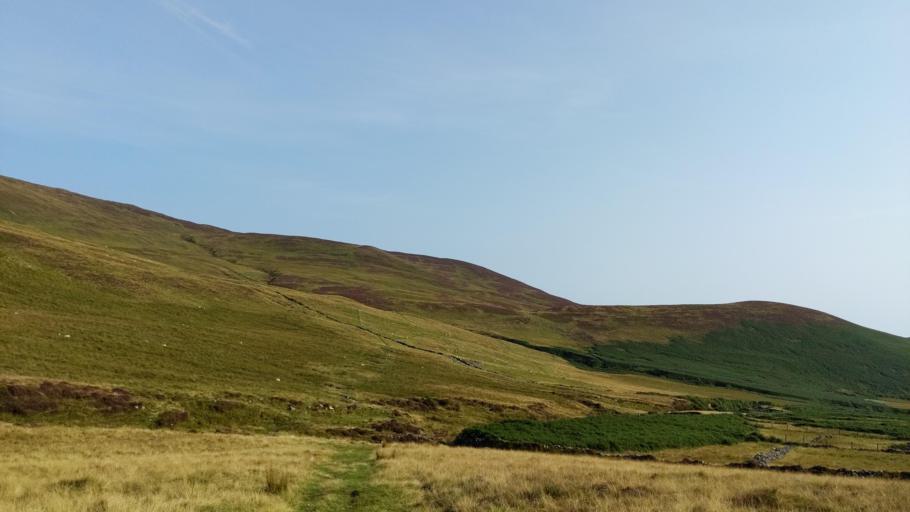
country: GB
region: Northern Ireland
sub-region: Down District
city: Warrenpoint
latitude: 54.0671
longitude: -6.3246
